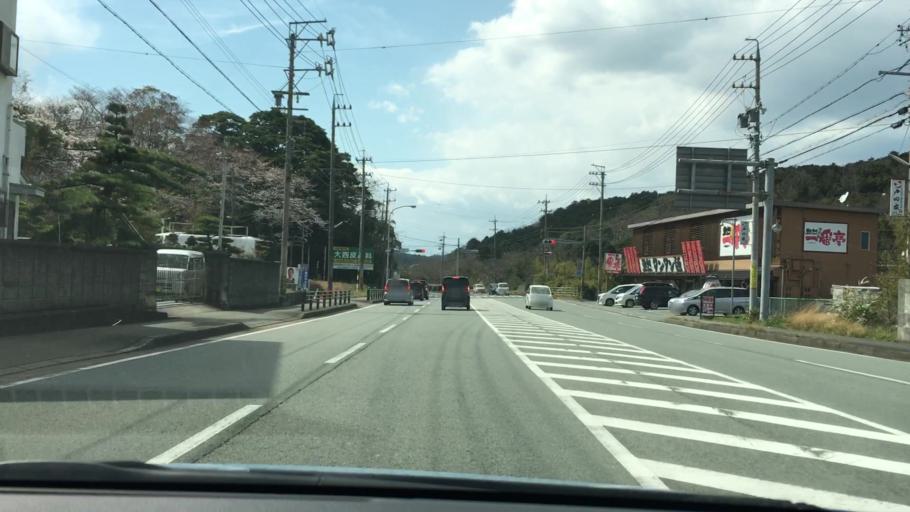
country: JP
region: Mie
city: Toba
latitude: 34.4864
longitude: 136.8325
